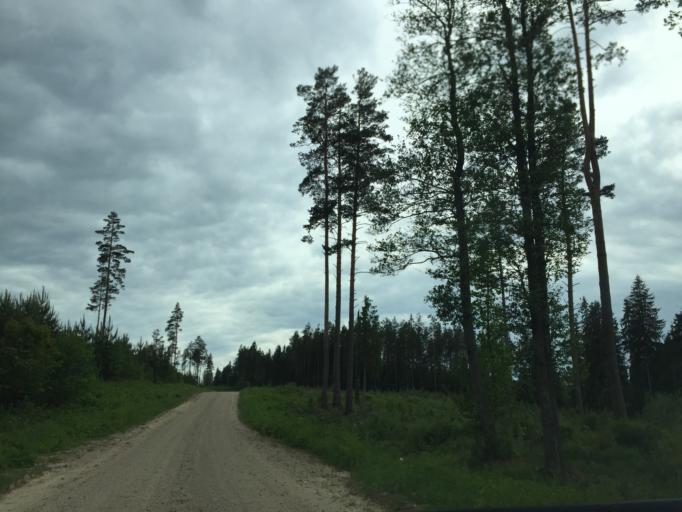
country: LV
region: Aglona
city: Aglona
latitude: 56.1502
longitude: 27.2232
